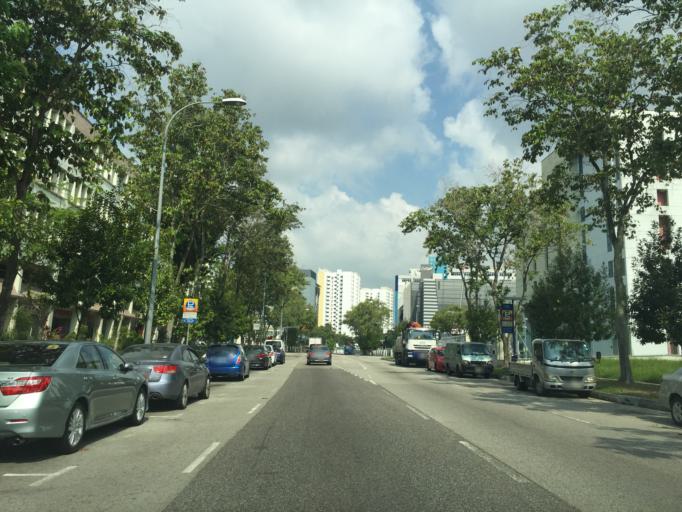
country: SG
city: Singapore
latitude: 1.3312
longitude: 103.8927
